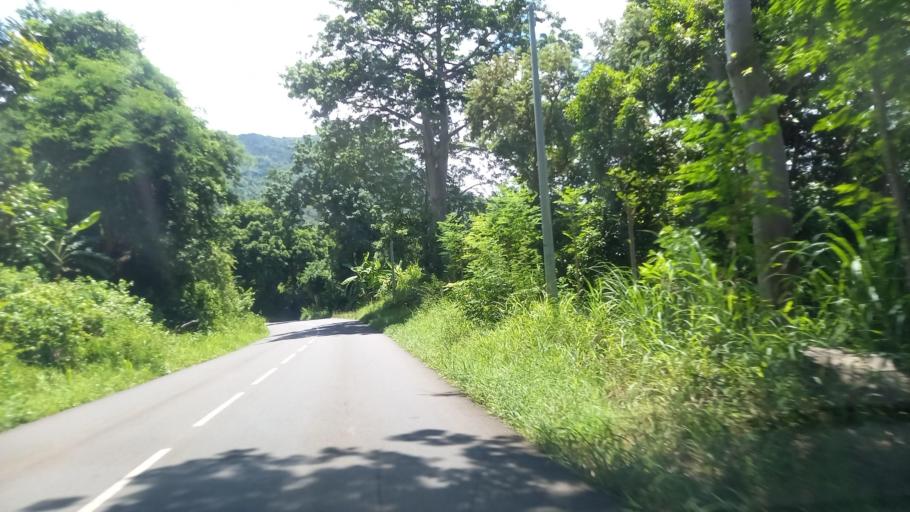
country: YT
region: Sada
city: Sada
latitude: -12.8619
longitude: 45.1088
